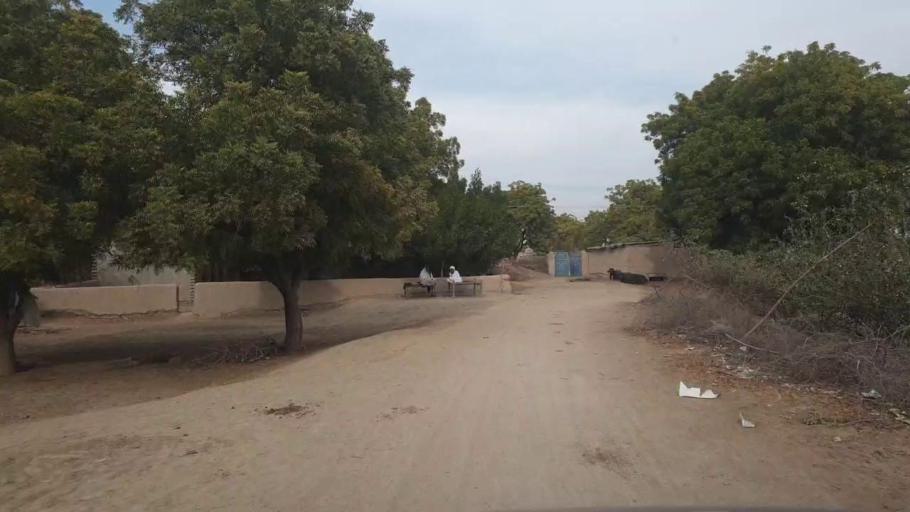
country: PK
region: Sindh
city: Shahpur Chakar
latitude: 26.1160
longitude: 68.5194
